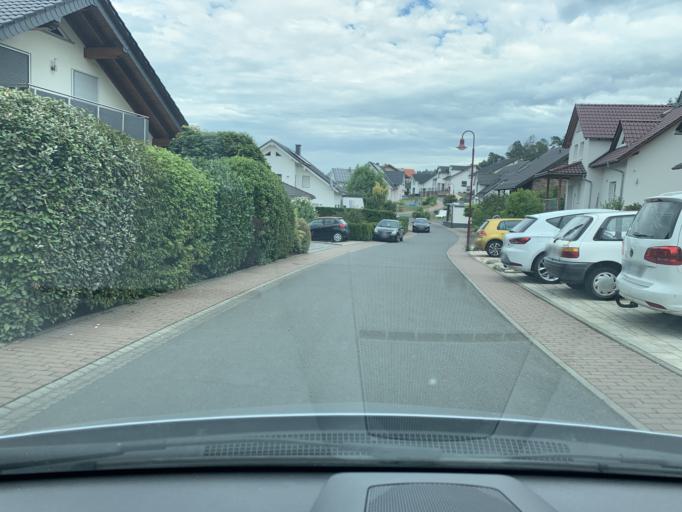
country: DE
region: Hesse
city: Wetter
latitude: 50.8589
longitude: 8.7470
